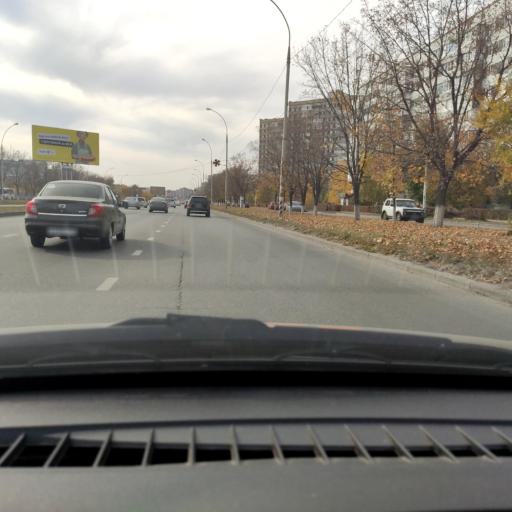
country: RU
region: Samara
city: Tol'yatti
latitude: 53.5275
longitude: 49.3326
